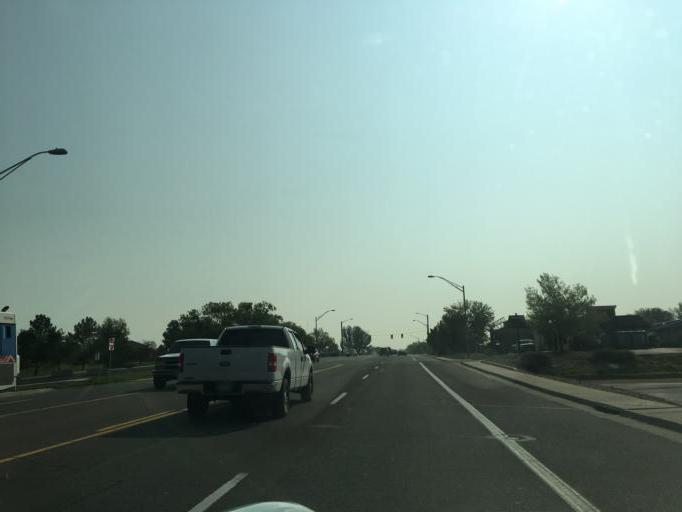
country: US
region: Colorado
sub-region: Adams County
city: Brighton
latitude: 39.9867
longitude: -104.7987
